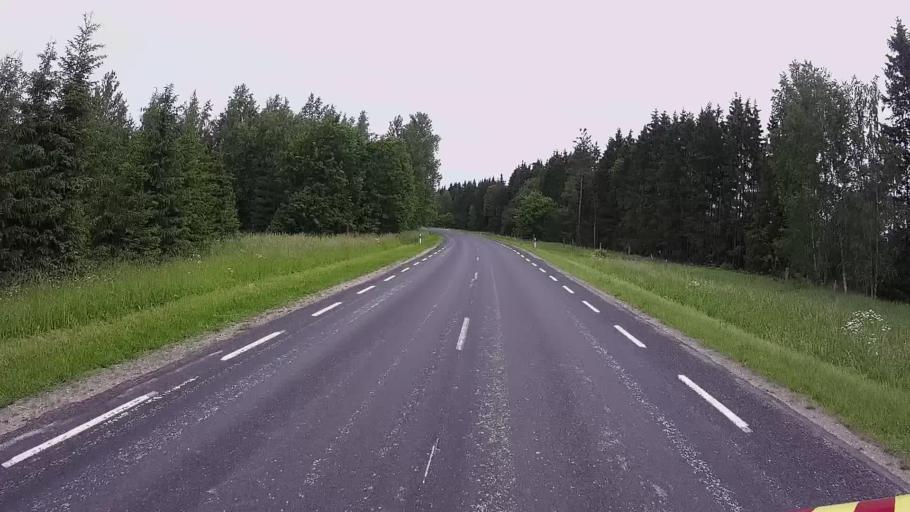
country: EE
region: Viljandimaa
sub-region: Karksi vald
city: Karksi-Nuia
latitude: 58.2027
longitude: 25.6195
